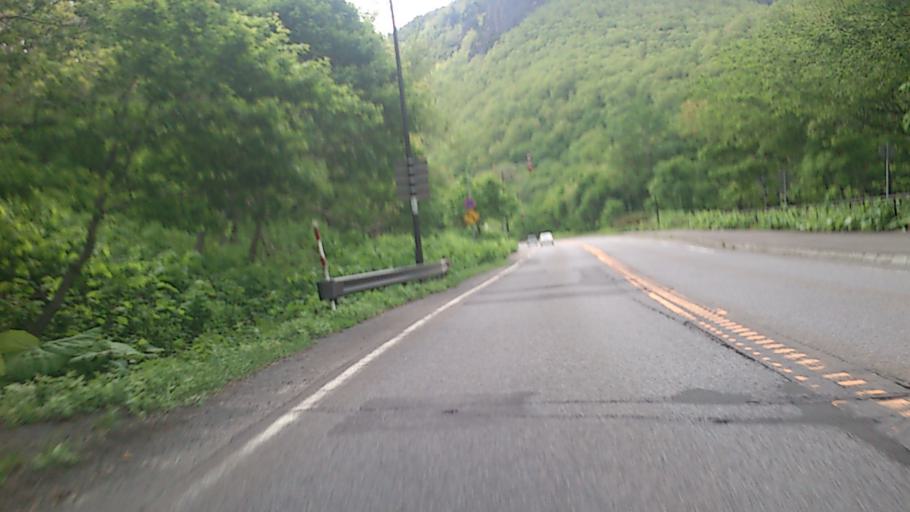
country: JP
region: Hokkaido
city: Kamikawa
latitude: 43.7275
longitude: 142.9545
